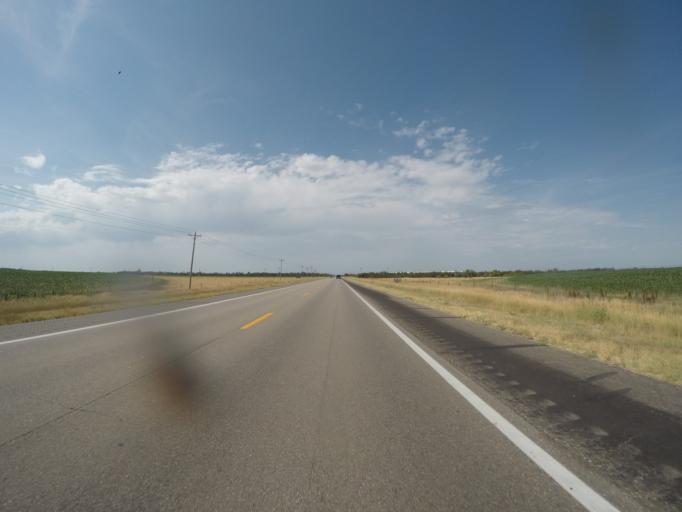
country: US
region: Nebraska
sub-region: Kearney County
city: Minden
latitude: 40.6239
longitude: -98.9515
